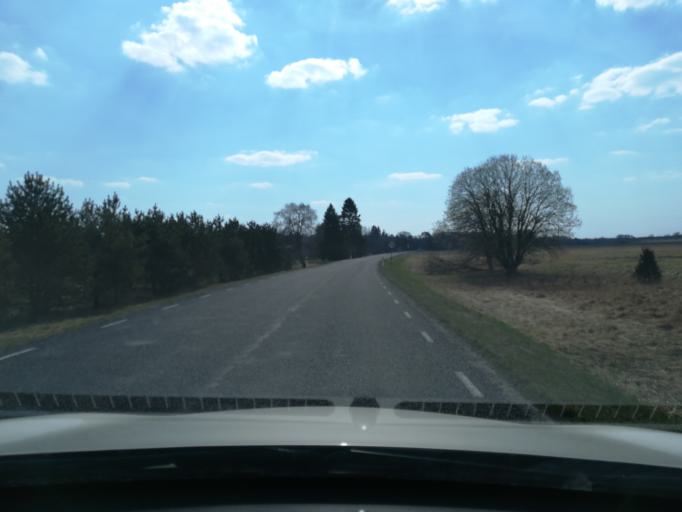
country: EE
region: Harju
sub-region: Keila linn
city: Keila
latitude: 59.3993
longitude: 24.4138
